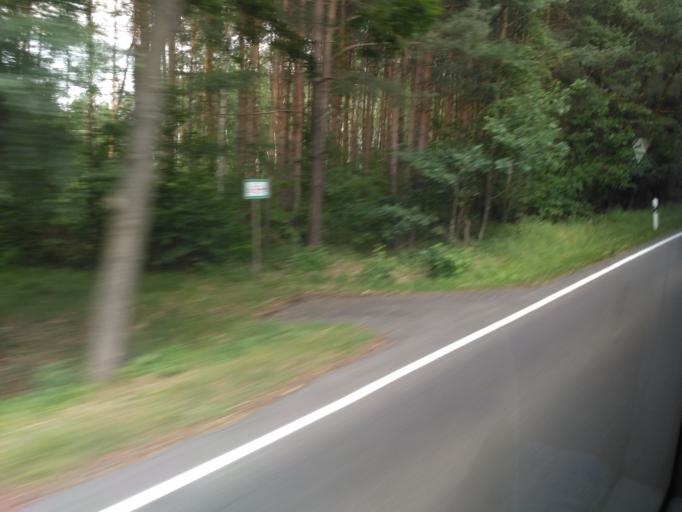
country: DE
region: Saxony
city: Coswig
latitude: 51.1620
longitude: 13.6059
